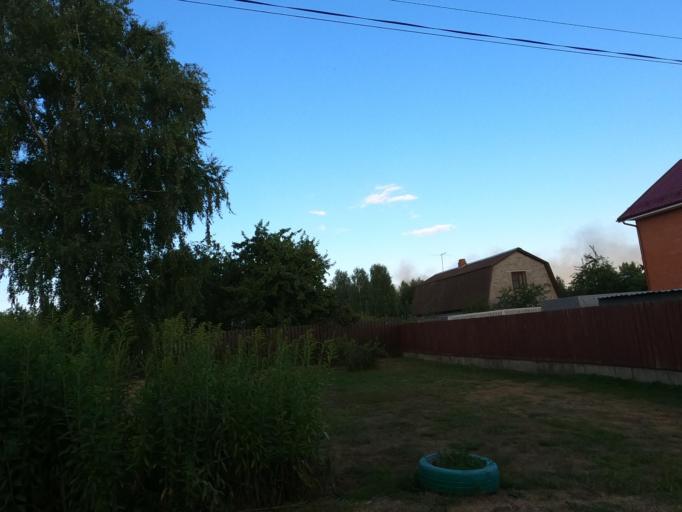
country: RU
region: Moskovskaya
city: Ashitkovo
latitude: 55.4175
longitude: 38.5798
